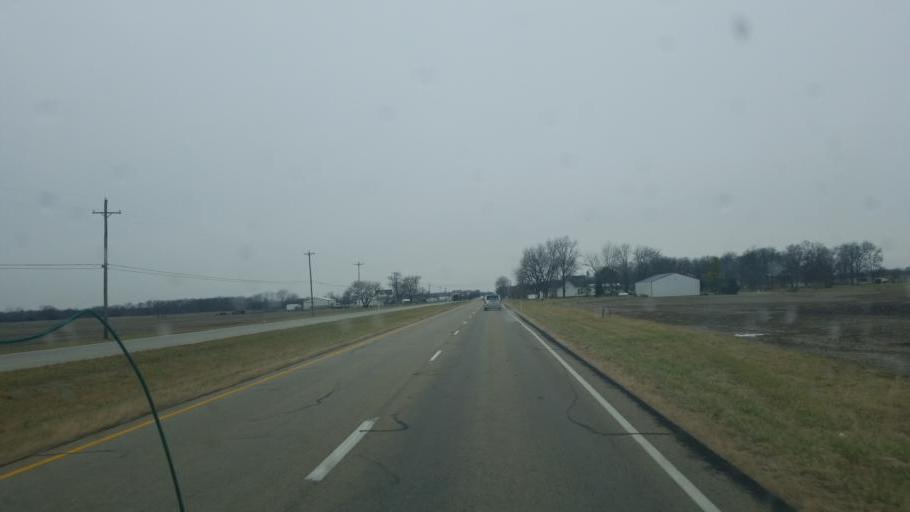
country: US
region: Indiana
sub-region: Henry County
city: Knightstown
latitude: 39.7924
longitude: -85.5844
